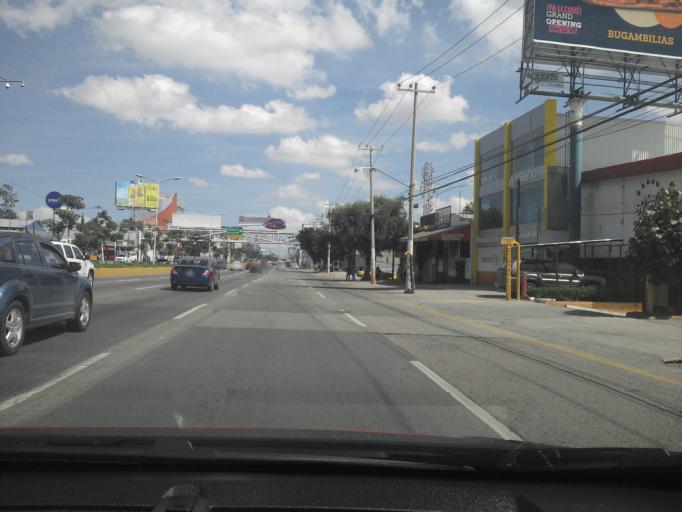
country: MX
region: Jalisco
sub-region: Tlajomulco de Zuniga
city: La Tijera
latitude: 20.6032
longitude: -103.4338
